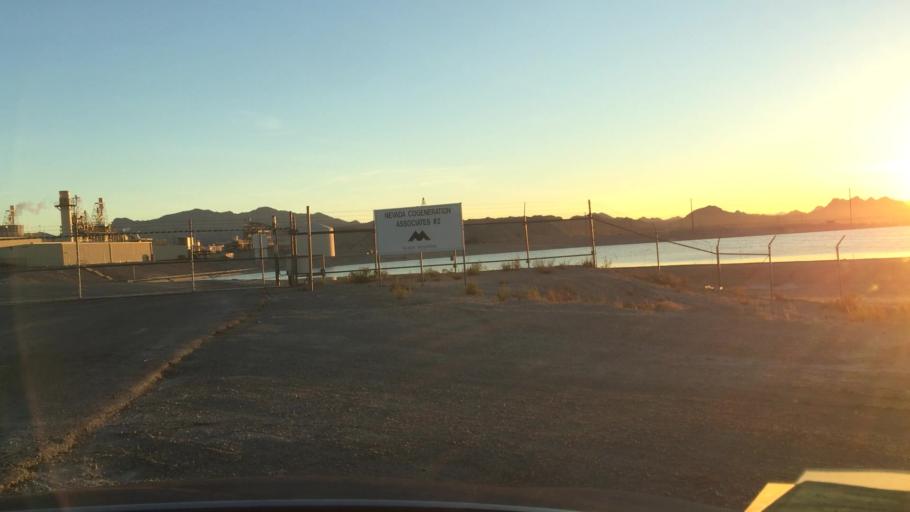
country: US
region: Nevada
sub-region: Clark County
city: Nellis Air Force Base
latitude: 36.2231
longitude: -114.8813
